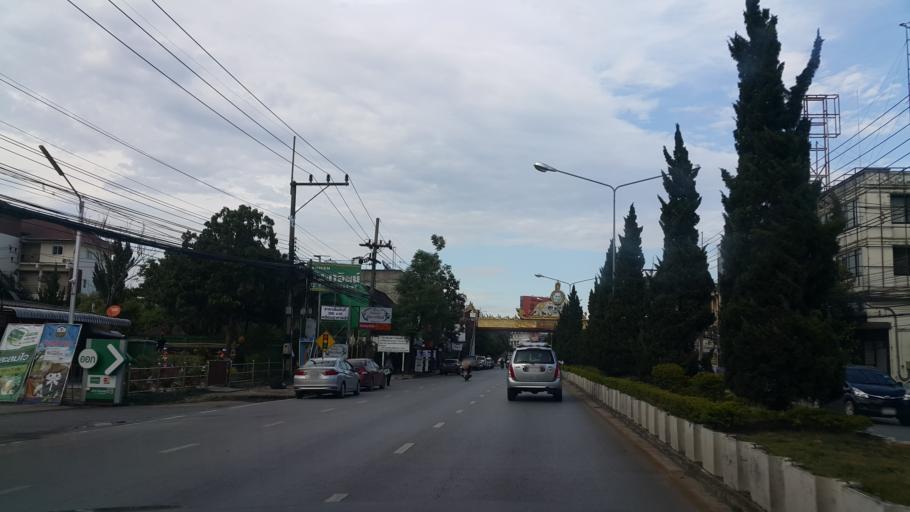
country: TH
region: Chiang Rai
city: Chiang Rai
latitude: 19.9139
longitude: 99.8435
